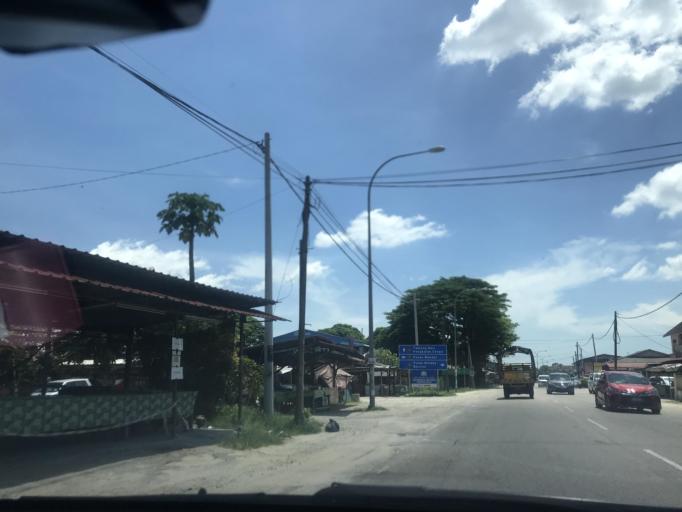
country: MY
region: Kelantan
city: Kota Bharu
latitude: 6.1216
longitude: 102.2711
